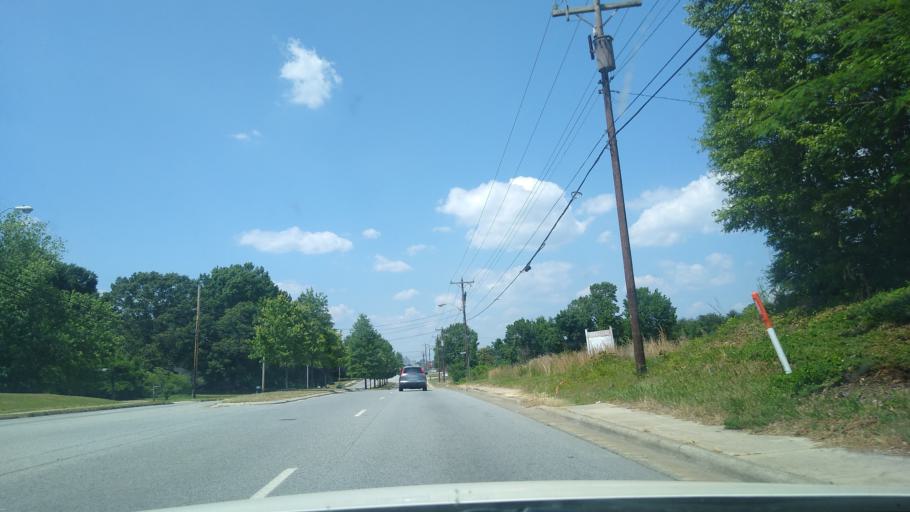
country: US
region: North Carolina
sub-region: Guilford County
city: Greensboro
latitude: 36.0237
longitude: -79.7916
